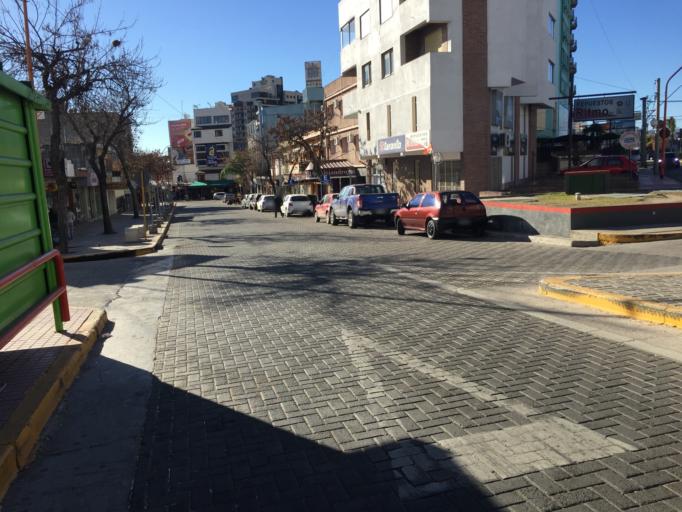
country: AR
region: Cordoba
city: Villa Carlos Paz
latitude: -31.4229
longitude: -64.4955
